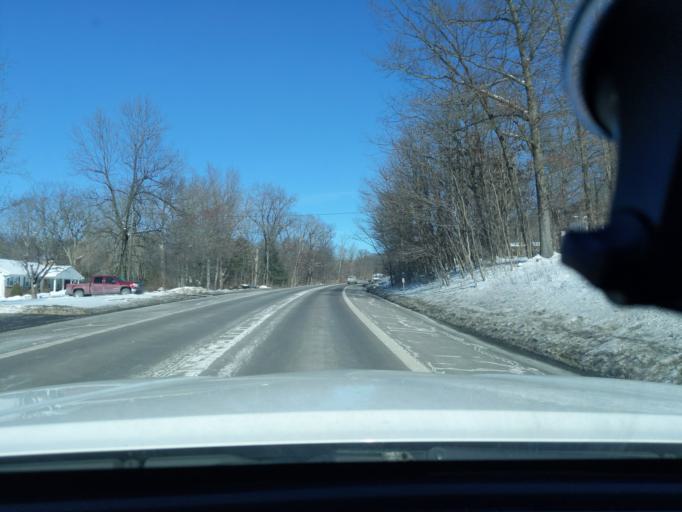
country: US
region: Maryland
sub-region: Allegany County
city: Frostburg
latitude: 39.6062
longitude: -78.9175
